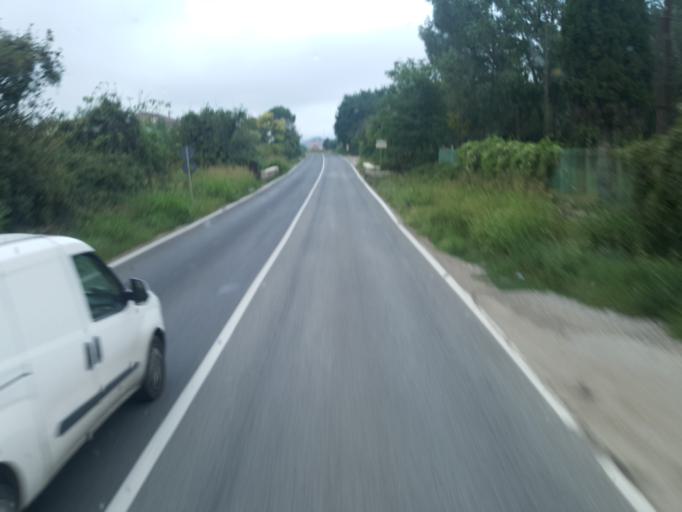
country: IT
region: Campania
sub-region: Provincia di Caserta
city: Sparanise
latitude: 41.1751
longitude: 14.1256
